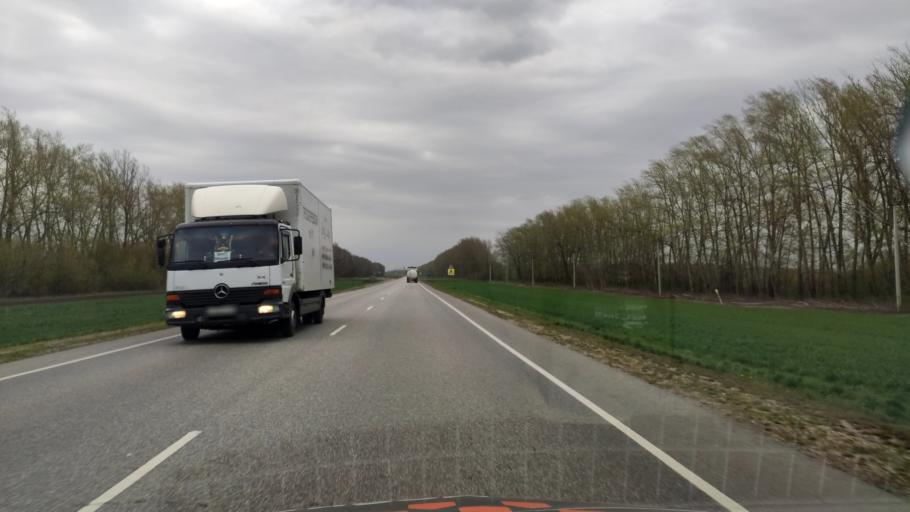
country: RU
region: Kursk
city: Olym
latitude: 51.5499
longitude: 38.1762
